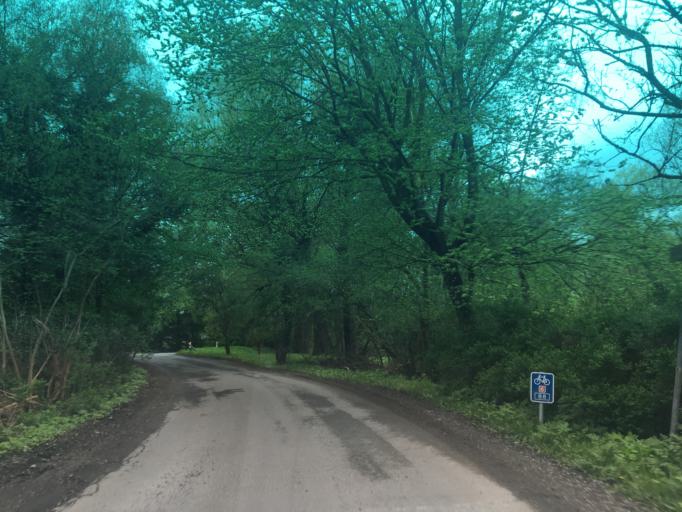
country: DK
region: Zealand
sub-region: Ringsted Kommune
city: Ringsted
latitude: 55.4131
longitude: 11.7059
